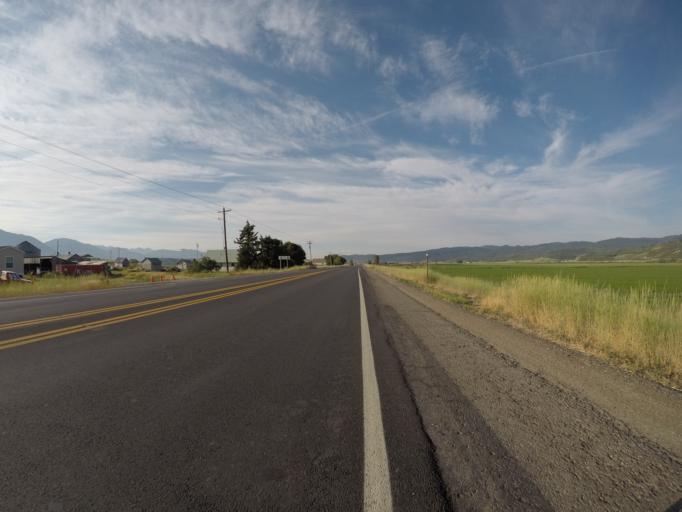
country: US
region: Wyoming
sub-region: Lincoln County
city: Afton
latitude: 42.9664
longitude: -111.0124
